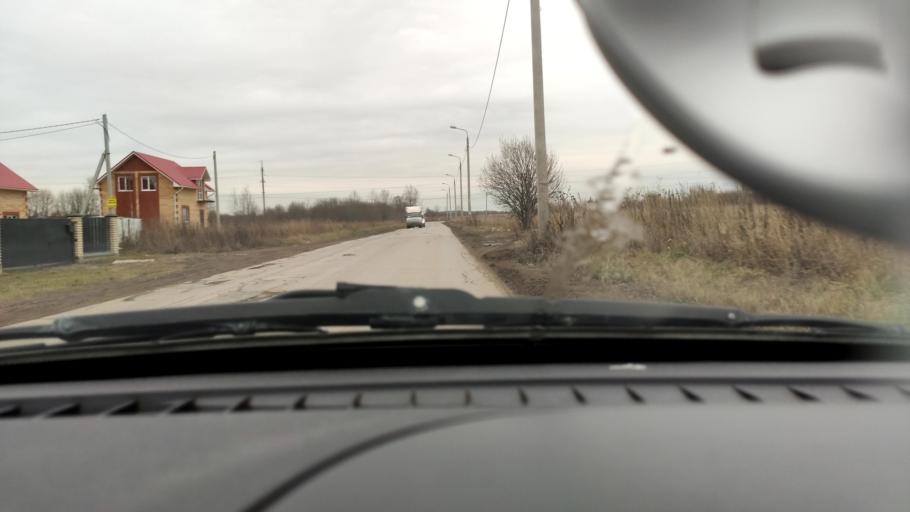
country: RU
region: Perm
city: Perm
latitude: 58.0205
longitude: 56.3357
